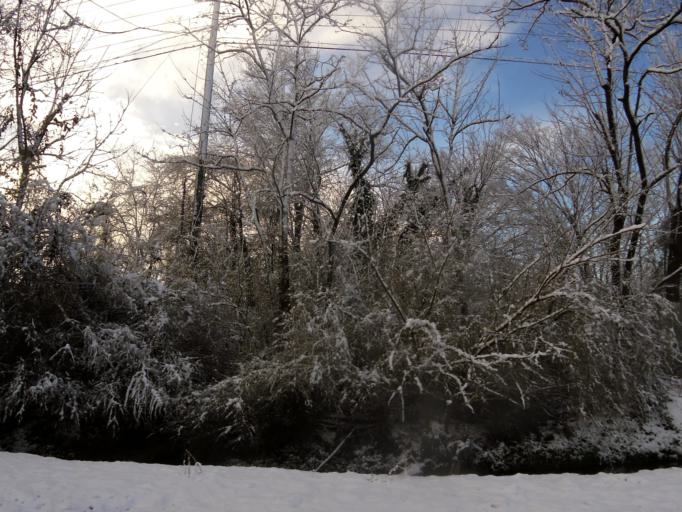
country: US
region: North Carolina
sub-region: Nash County
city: Rocky Mount
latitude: 35.9164
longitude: -77.8066
